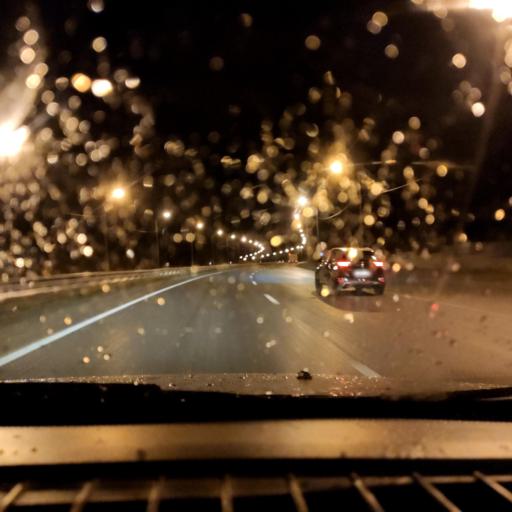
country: RU
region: Samara
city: Zhigulevsk
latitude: 53.5345
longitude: 49.5164
